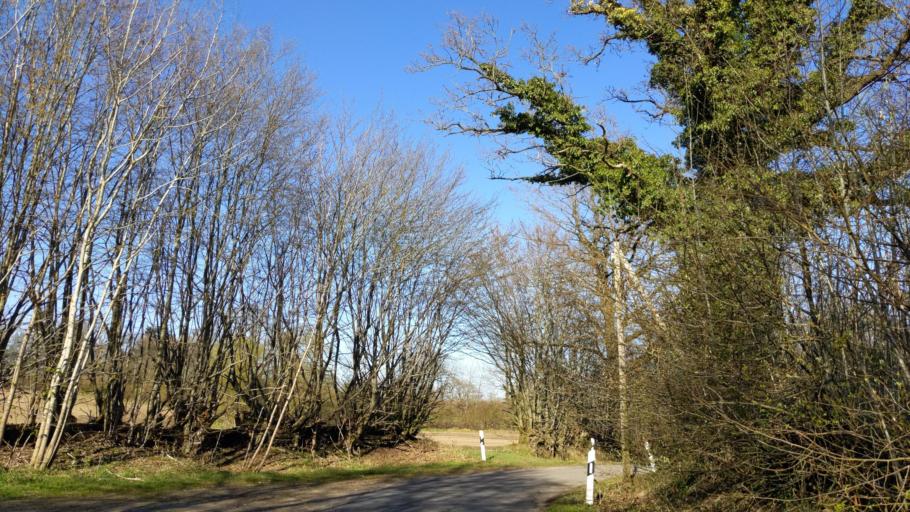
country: DE
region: Schleswig-Holstein
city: Scharbeutz
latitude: 54.0229
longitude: 10.7251
